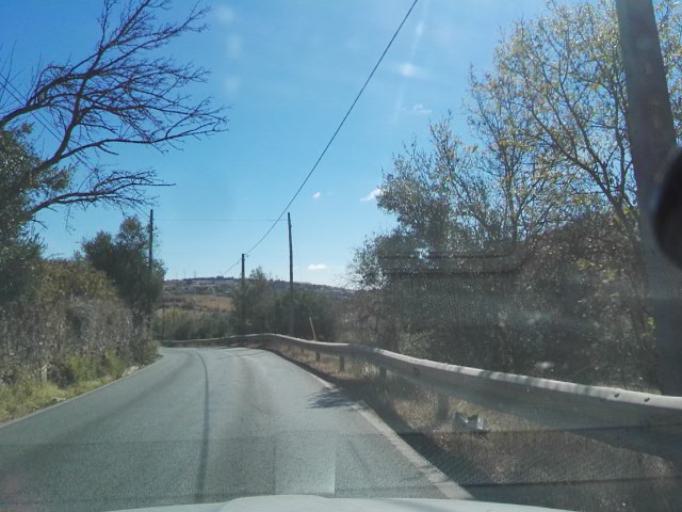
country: PT
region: Lisbon
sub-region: Vila Franca de Xira
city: Sao Joao dos Montes
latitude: 38.9478
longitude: -9.0489
